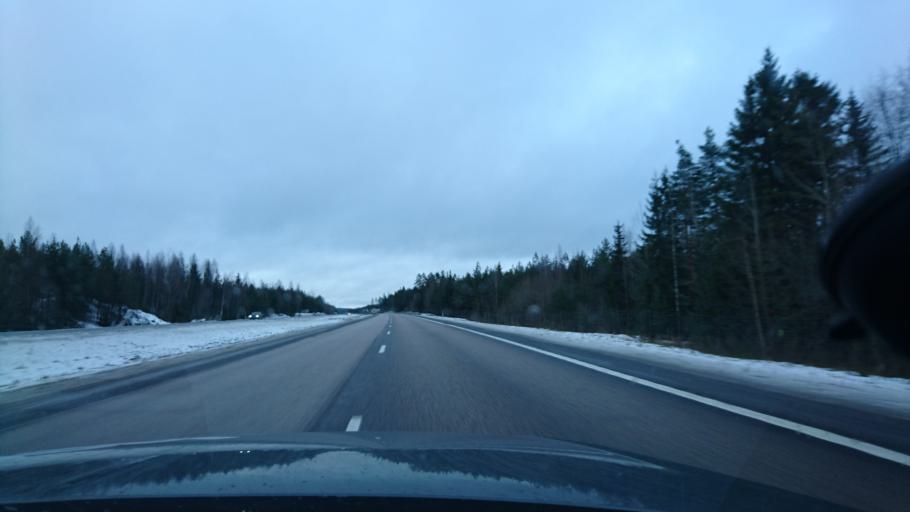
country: FI
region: Uusimaa
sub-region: Porvoo
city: Pukkila
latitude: 60.7430
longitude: 25.4543
